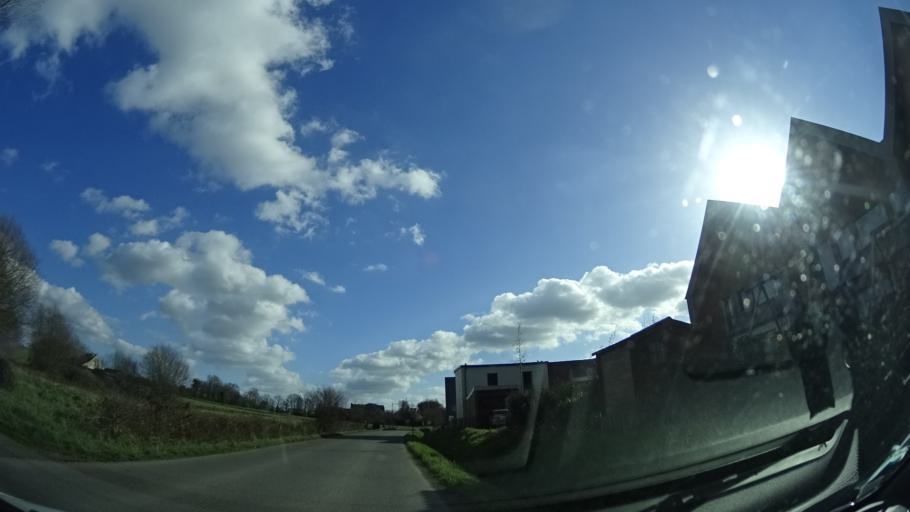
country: FR
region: Brittany
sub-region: Departement d'Ille-et-Vilaine
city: Pace
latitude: 48.1567
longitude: -1.7590
